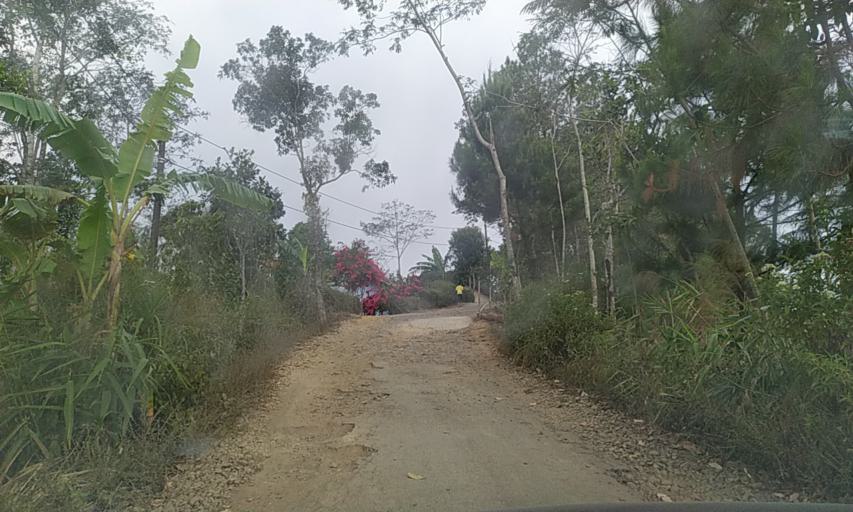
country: ID
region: Central Java
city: Randudongkal
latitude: -7.1881
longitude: 109.4212
